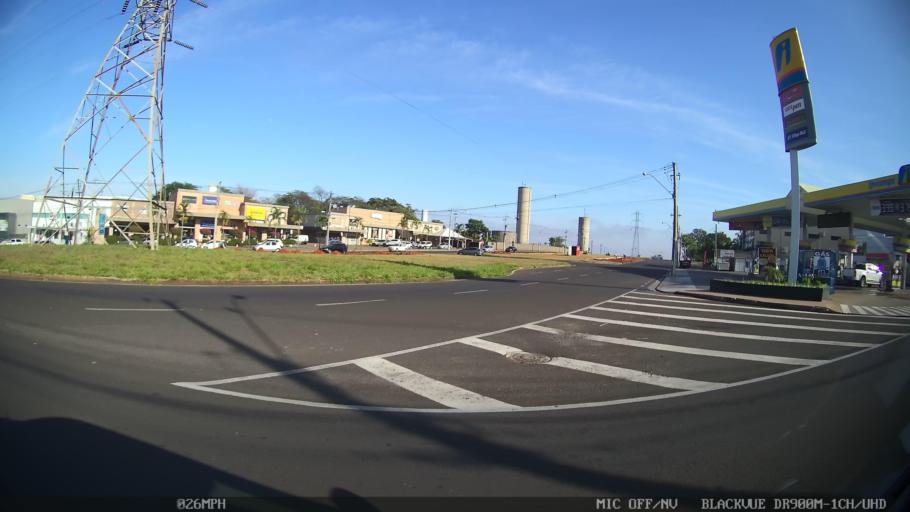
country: BR
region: Sao Paulo
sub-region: Sao Jose Do Rio Preto
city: Sao Jose do Rio Preto
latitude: -20.7793
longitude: -49.3424
